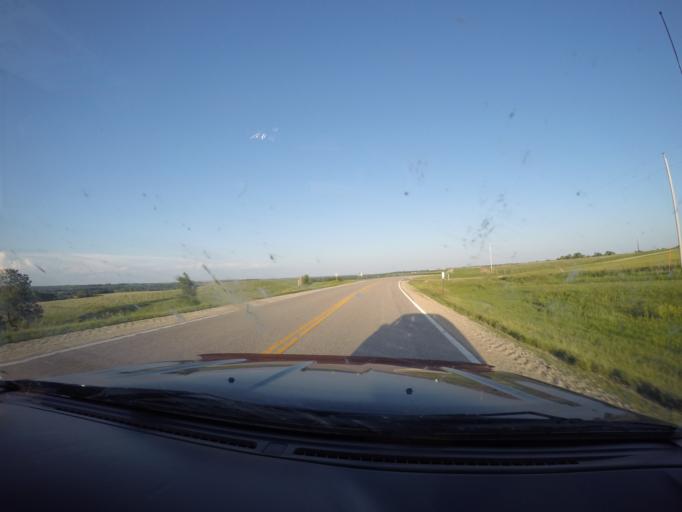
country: US
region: Kansas
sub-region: Marshall County
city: Blue Rapids
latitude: 39.6971
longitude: -96.7941
